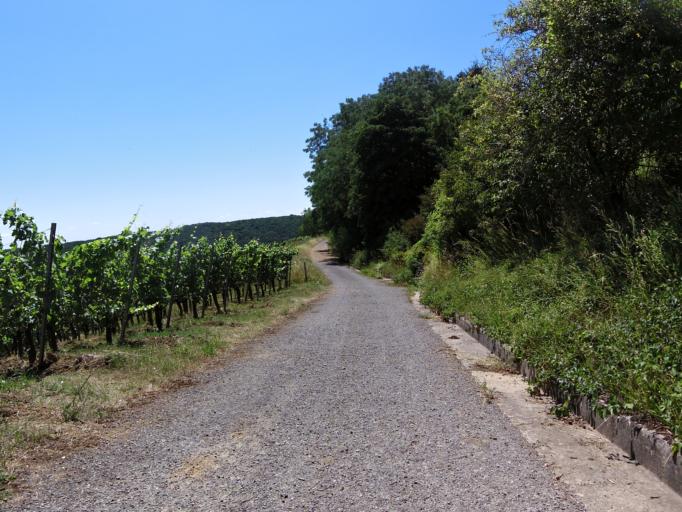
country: DE
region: Bavaria
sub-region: Regierungsbezirk Unterfranken
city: Gerbrunn
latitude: 49.7621
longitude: 10.0063
